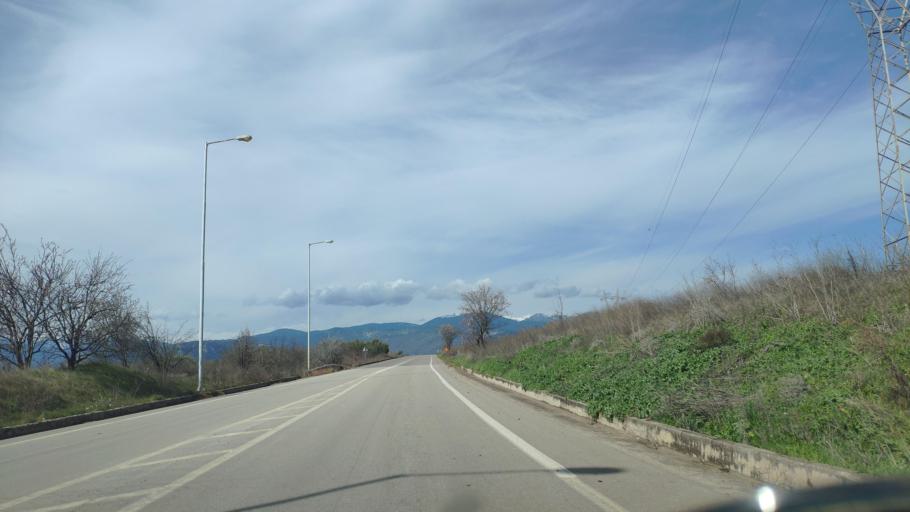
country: GR
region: Central Greece
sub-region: Nomos Fthiotidos
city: Amfikleia
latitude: 38.7091
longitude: 22.4875
